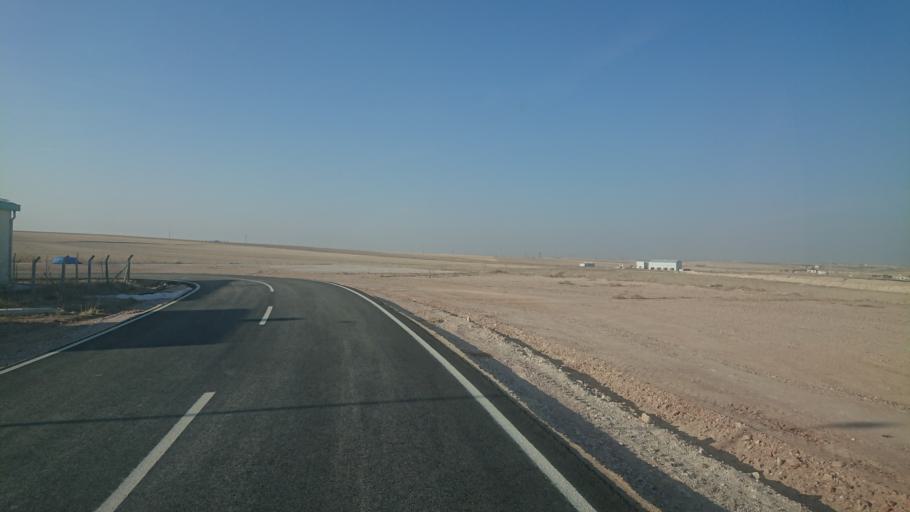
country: TR
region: Aksaray
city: Sultanhani
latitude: 38.0892
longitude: 33.6087
